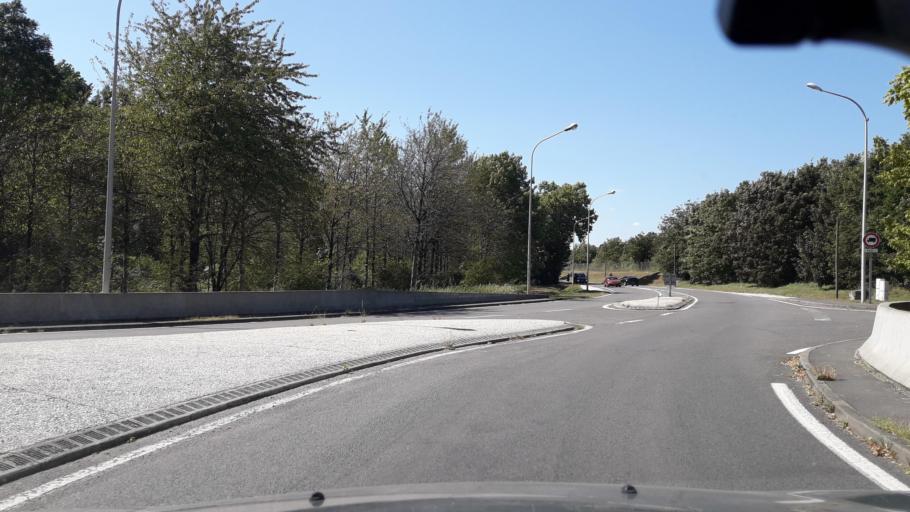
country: FR
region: Poitou-Charentes
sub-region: Departement de la Charente
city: Gond-Pontouvre
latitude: 45.6870
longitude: 0.1852
